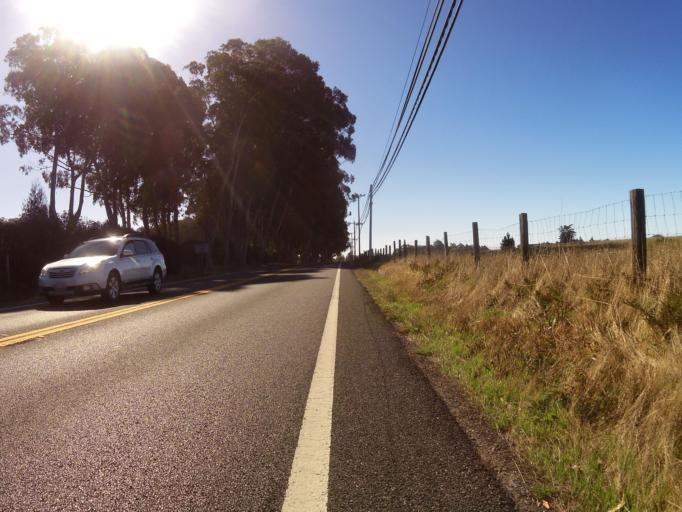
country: US
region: California
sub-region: Mendocino County
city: Fort Bragg
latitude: 39.2841
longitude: -123.7933
